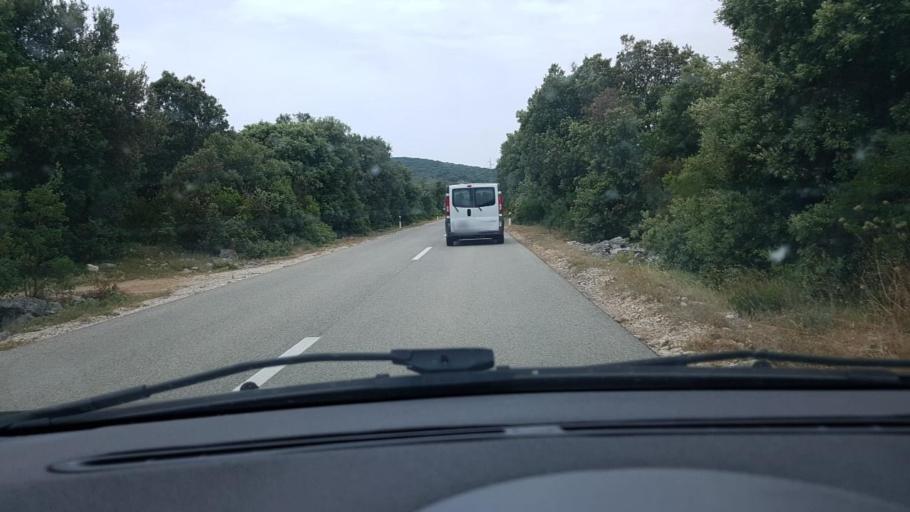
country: HR
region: Dubrovacko-Neretvanska
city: Smokvica
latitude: 42.9483
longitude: 16.9994
